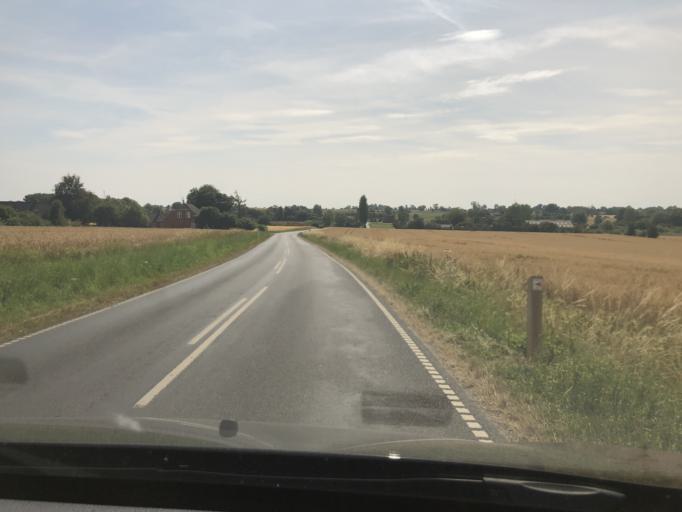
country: DK
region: South Denmark
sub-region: AEro Kommune
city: AEroskobing
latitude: 54.8747
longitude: 10.3972
